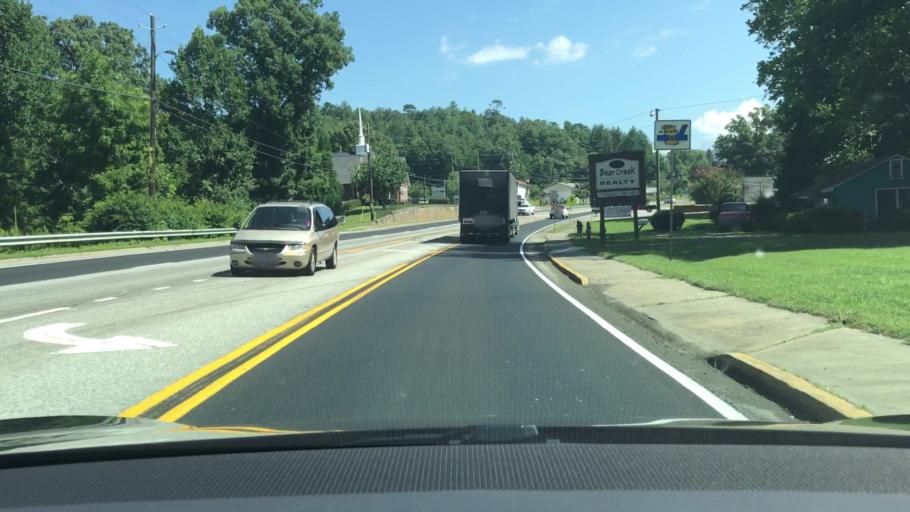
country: US
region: Georgia
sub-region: Rabun County
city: Mountain City
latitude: 34.9684
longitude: -83.3882
